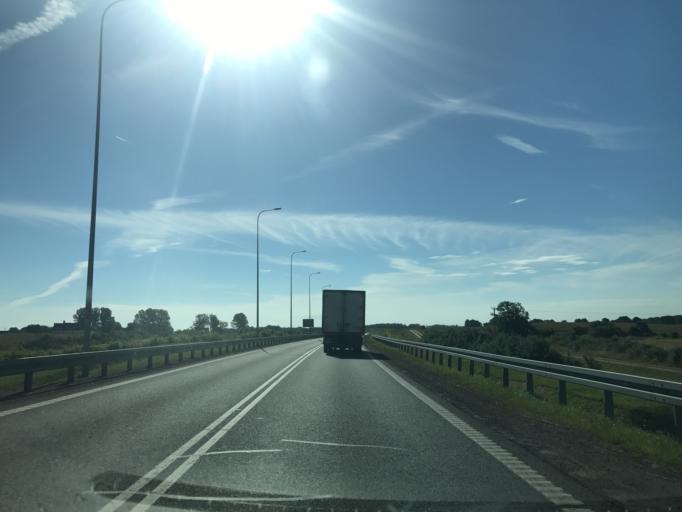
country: PL
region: Pomeranian Voivodeship
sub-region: Powiat chojnicki
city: Chojnice
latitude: 53.6883
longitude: 17.4768
